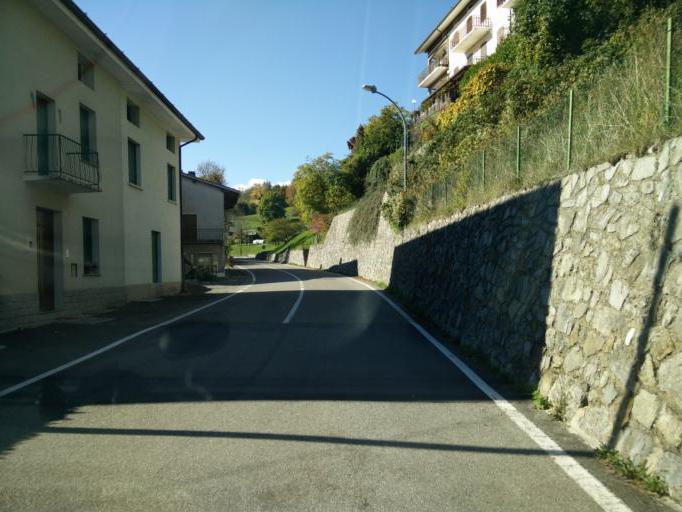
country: IT
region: Lombardy
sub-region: Provincia di Brescia
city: Capovalle
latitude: 45.7533
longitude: 10.5450
